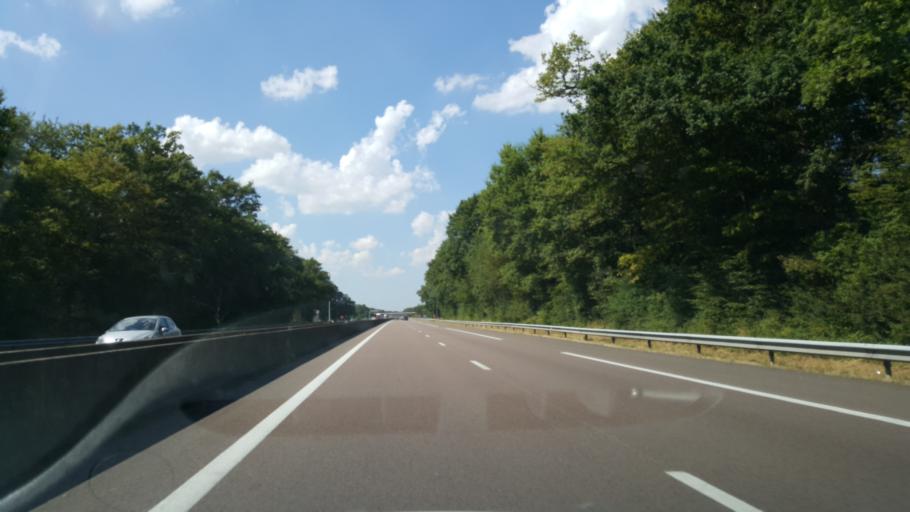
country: FR
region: Bourgogne
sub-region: Departement de la Cote-d'Or
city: Semur-en-Auxois
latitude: 47.3888
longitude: 4.3661
